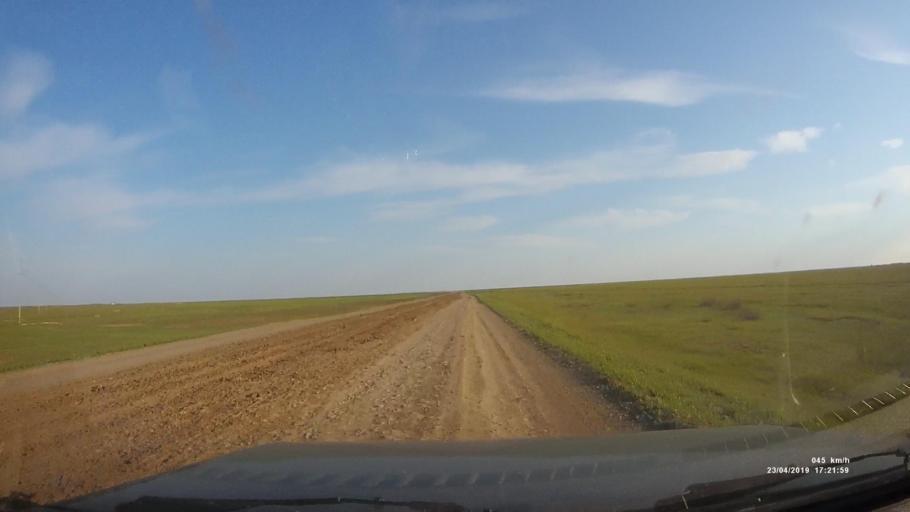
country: RU
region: Kalmykiya
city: Priyutnoye
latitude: 46.1720
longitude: 43.5060
